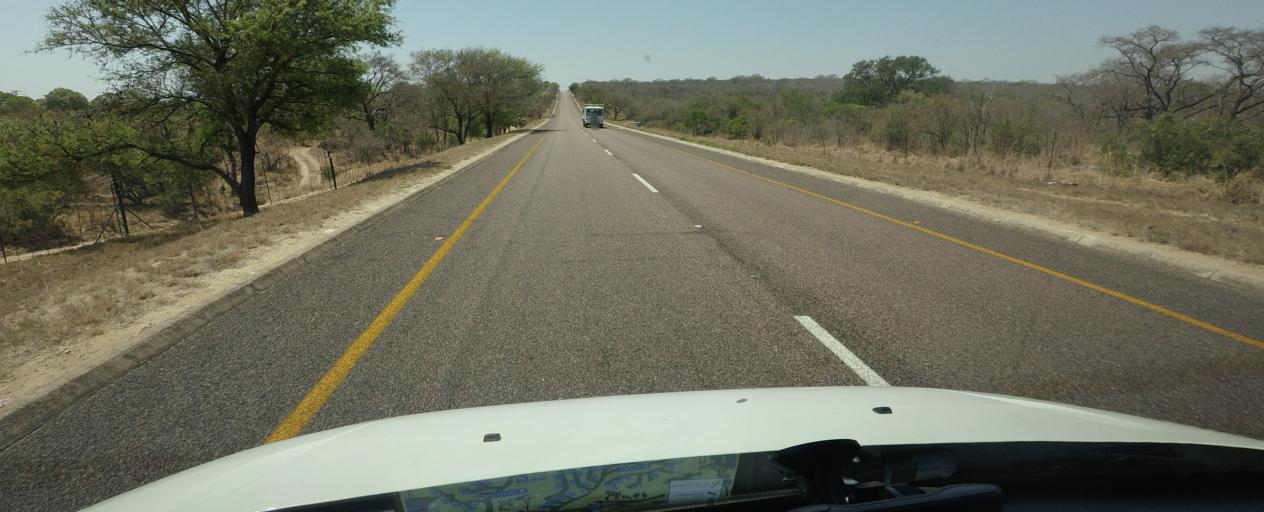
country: ZA
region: Limpopo
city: Thulamahashi
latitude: -24.5549
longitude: 31.2418
